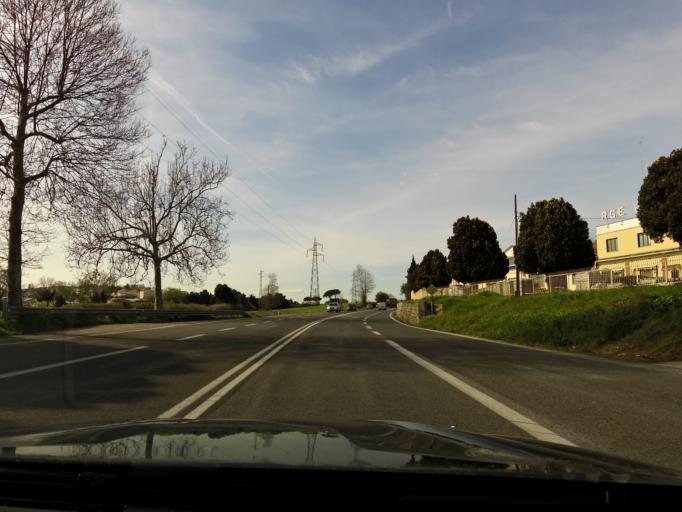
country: IT
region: The Marches
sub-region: Provincia di Ancona
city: Loreto Stazione
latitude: 43.4396
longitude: 13.6385
